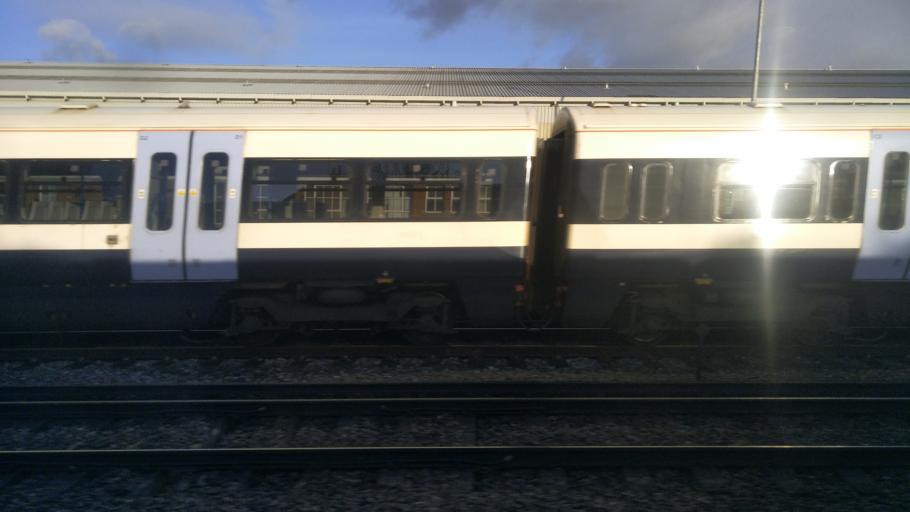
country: GB
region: England
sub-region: Greater London
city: Bromley
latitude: 51.4341
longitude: 0.0173
